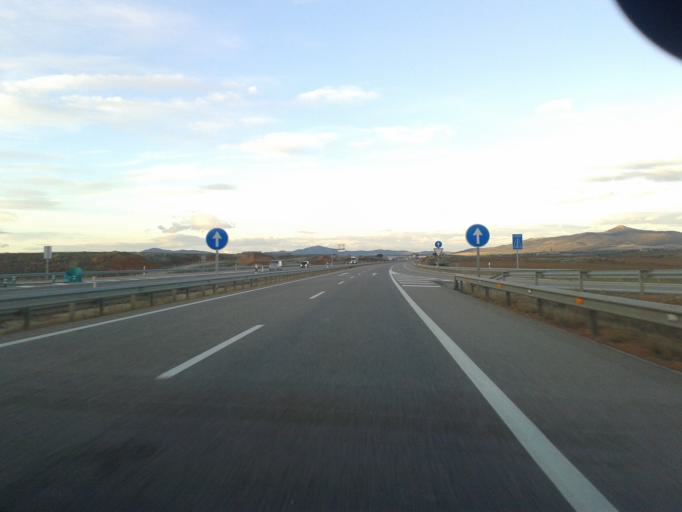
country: ES
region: Aragon
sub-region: Provincia de Zaragoza
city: Lechon
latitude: 41.0904
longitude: -1.2905
